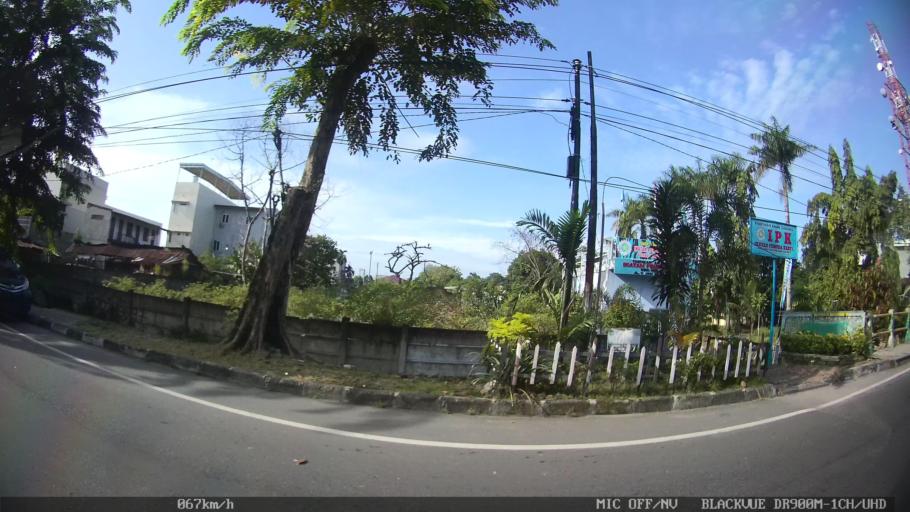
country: ID
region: North Sumatra
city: Medan
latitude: 3.6072
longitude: 98.6610
